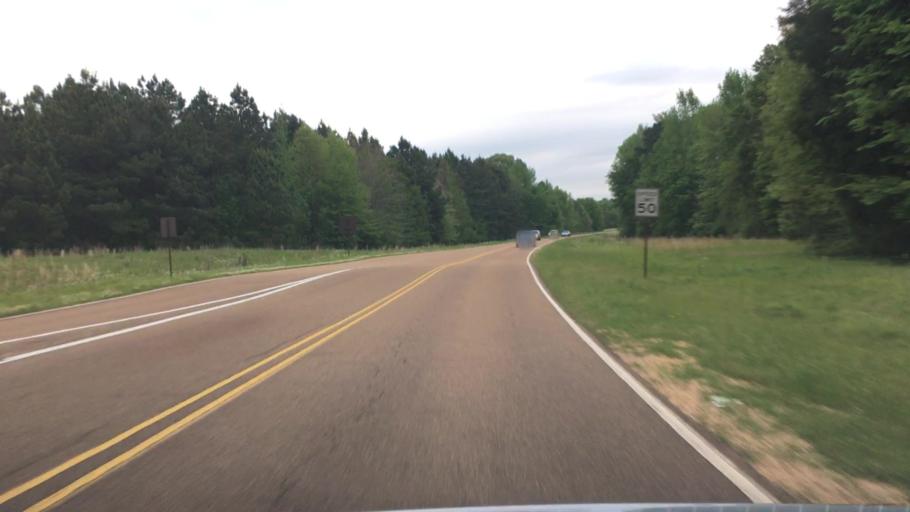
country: US
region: Mississippi
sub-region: Hinds County
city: Clinton
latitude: 32.3854
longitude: -90.2577
